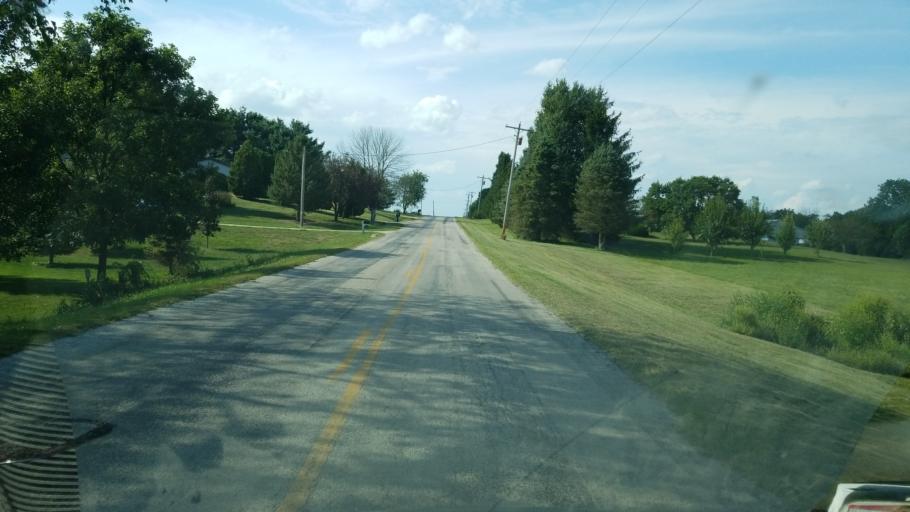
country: US
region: Ohio
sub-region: Marion County
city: Prospect
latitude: 40.5063
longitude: -83.2019
